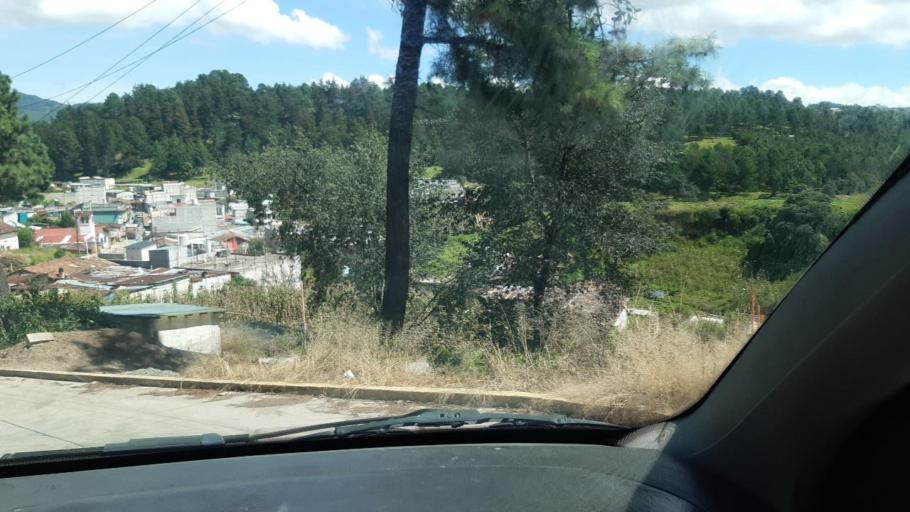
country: GT
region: Quetzaltenango
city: Salcaja
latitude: 14.8680
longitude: -91.4561
